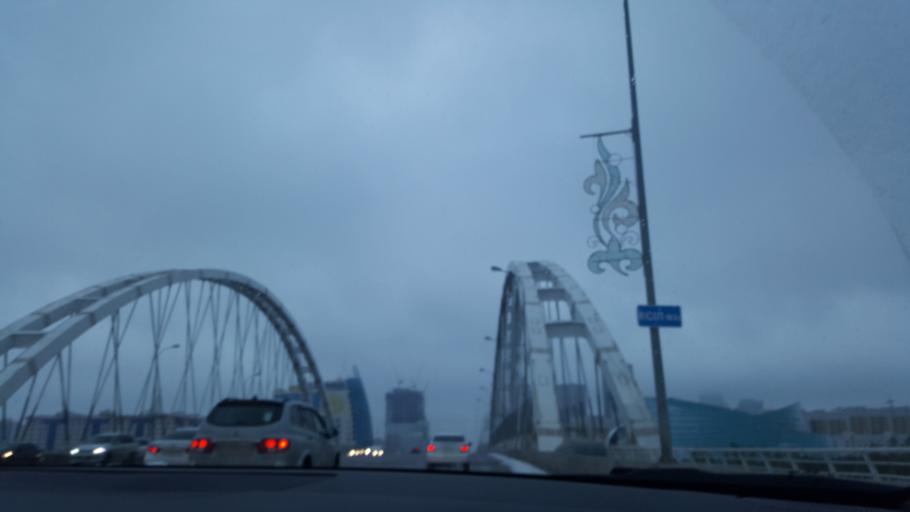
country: KZ
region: Astana Qalasy
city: Astana
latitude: 51.1204
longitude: 71.4476
